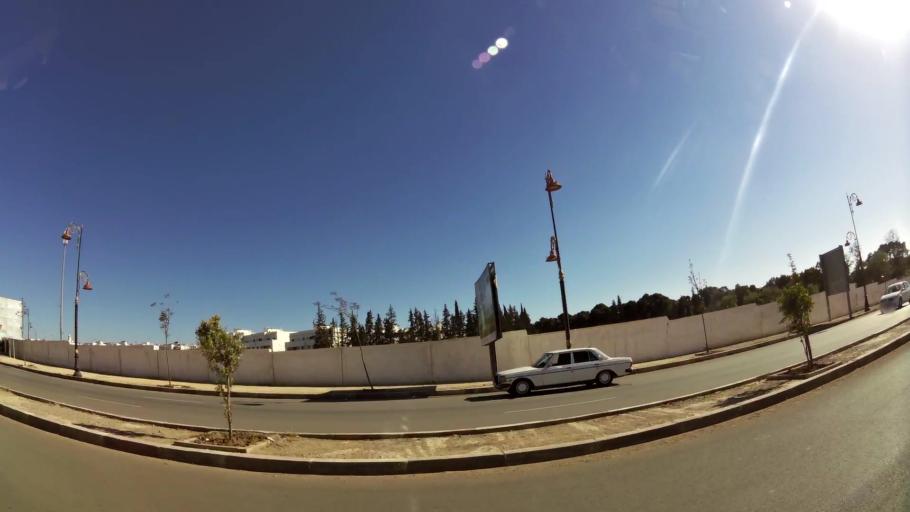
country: MA
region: Fes-Boulemane
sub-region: Fes
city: Fes
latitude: 33.9913
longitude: -5.0165
